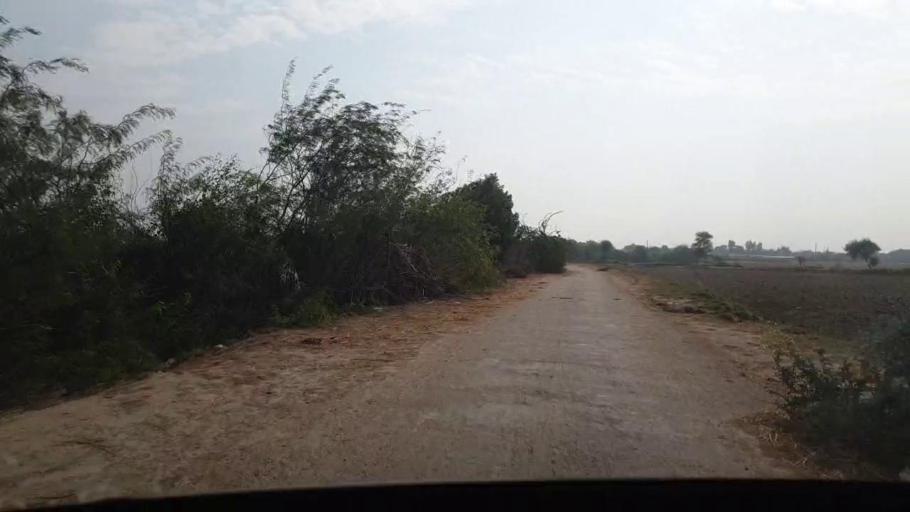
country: PK
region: Sindh
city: Chuhar Jamali
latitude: 24.3203
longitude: 67.9431
